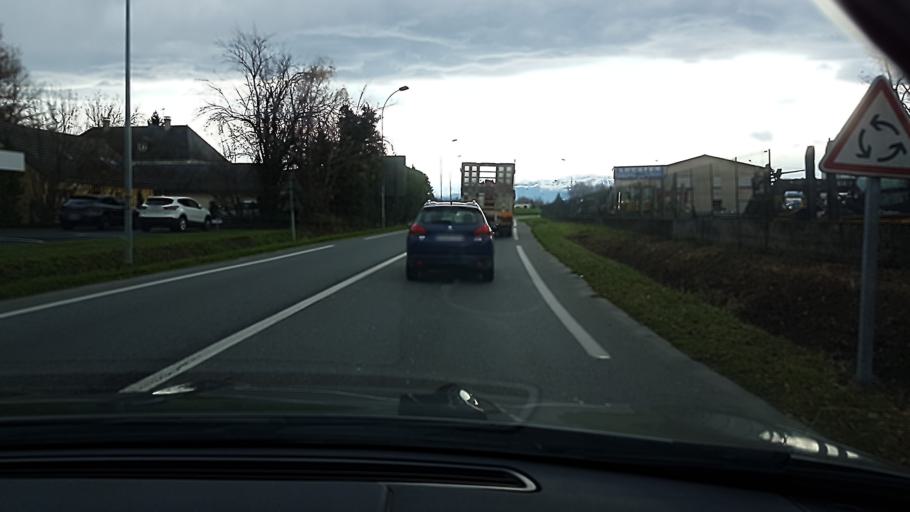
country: FR
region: Aquitaine
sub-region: Departement des Pyrenees-Atlantiques
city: Idron
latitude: 43.3008
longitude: -0.3075
